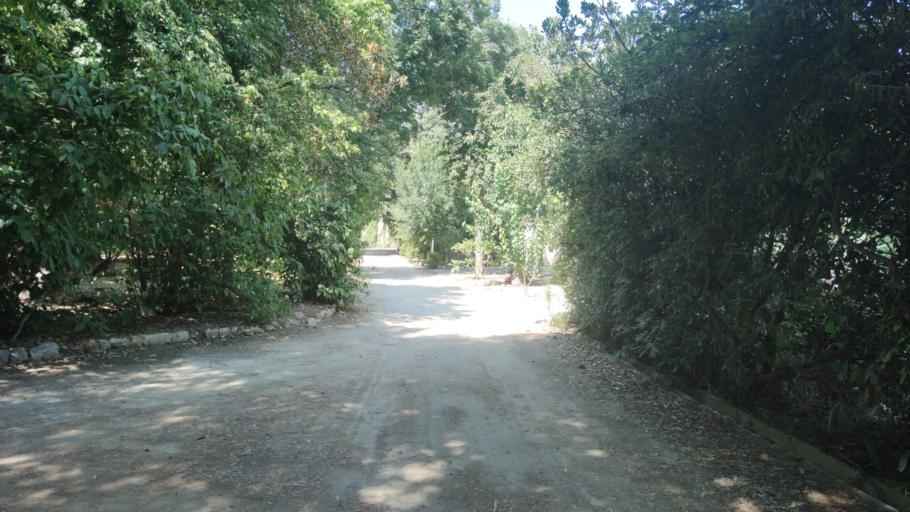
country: IT
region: Sicily
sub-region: Palermo
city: Palermo
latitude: 38.1095
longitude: 13.3750
